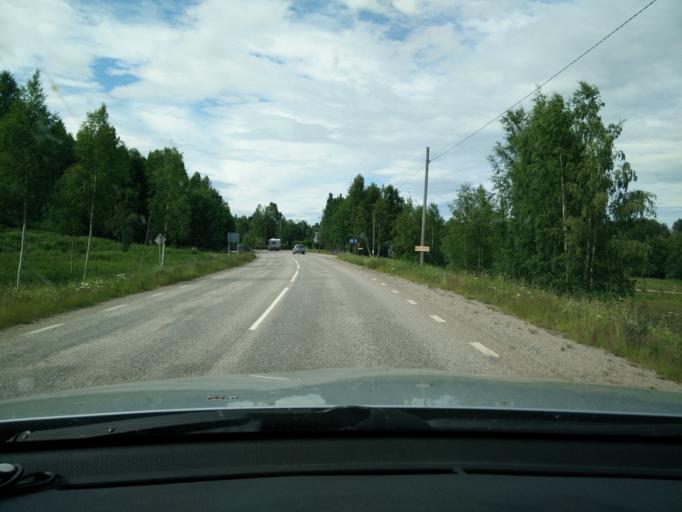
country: SE
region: Gaevleborg
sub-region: Nordanstigs Kommun
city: Bergsjoe
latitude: 61.9563
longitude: 17.0630
